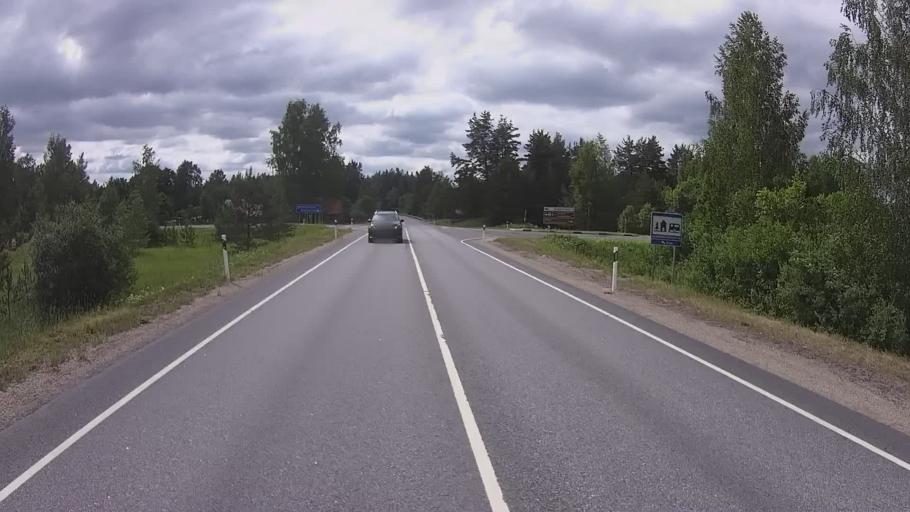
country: EE
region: Polvamaa
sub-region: Polva linn
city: Polva
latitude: 58.1248
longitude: 26.9555
